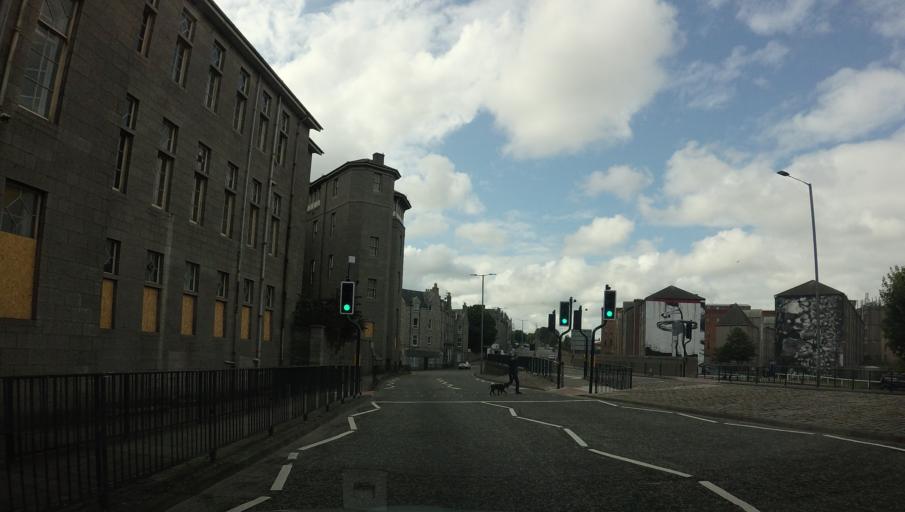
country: GB
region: Scotland
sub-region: Aberdeen City
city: Aberdeen
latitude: 57.1496
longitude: -2.1060
